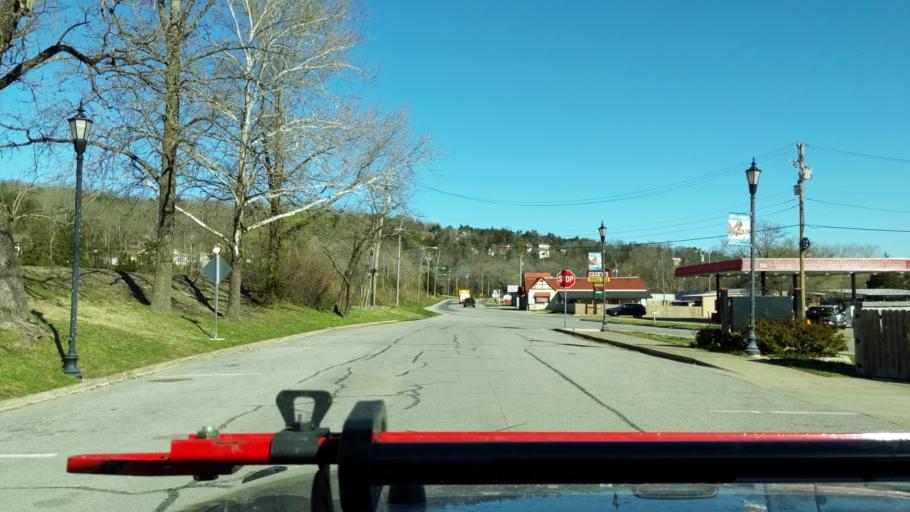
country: US
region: Missouri
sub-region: Taney County
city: Hollister
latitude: 36.6242
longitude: -93.2170
